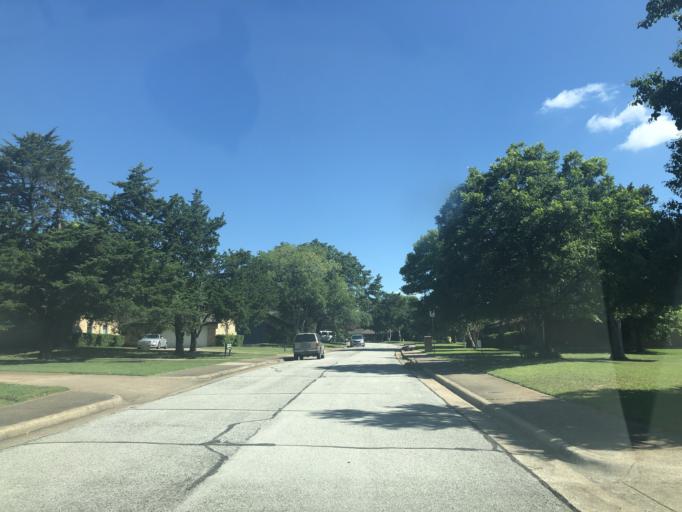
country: US
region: Texas
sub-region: Dallas County
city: Duncanville
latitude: 32.6422
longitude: -96.9403
